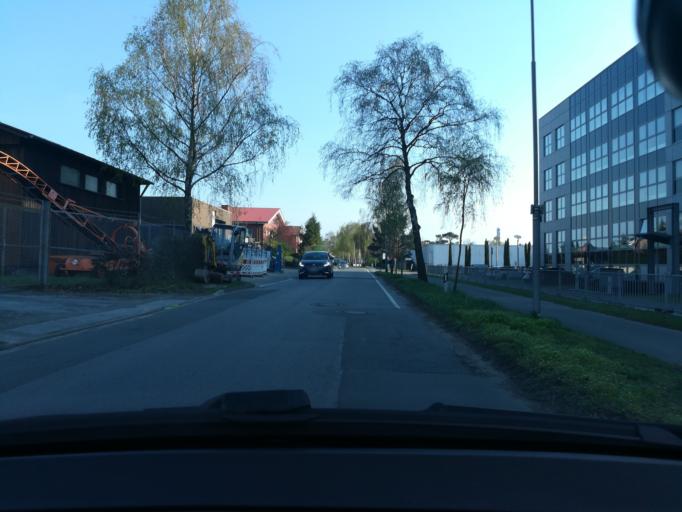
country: DE
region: North Rhine-Westphalia
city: Halle
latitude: 52.0479
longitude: 8.3751
